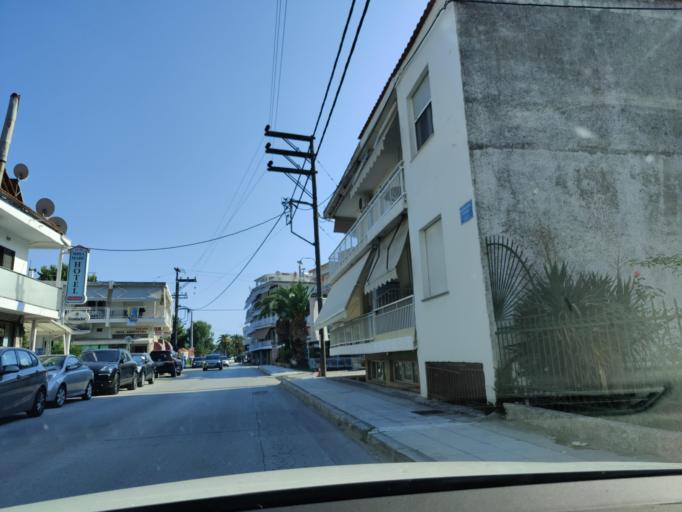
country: GR
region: East Macedonia and Thrace
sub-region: Nomos Kavalas
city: Nea Peramos
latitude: 40.8428
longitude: 24.3057
